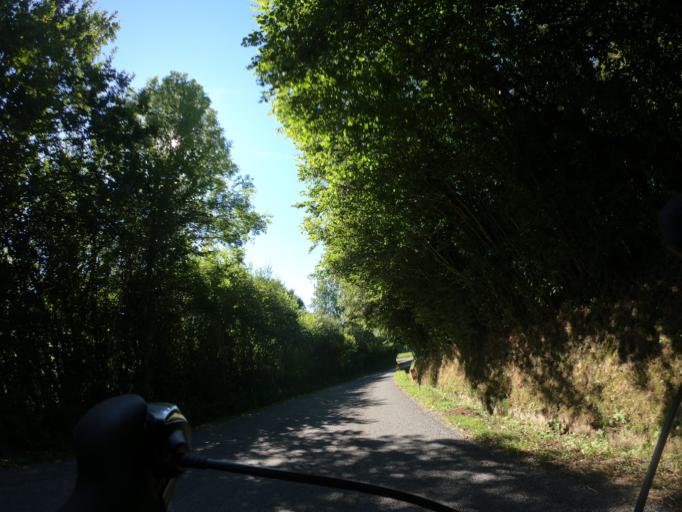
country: FR
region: Lower Normandy
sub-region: Departement de l'Orne
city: Saint-Denis-sur-Sarthon
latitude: 48.5485
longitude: -0.1097
